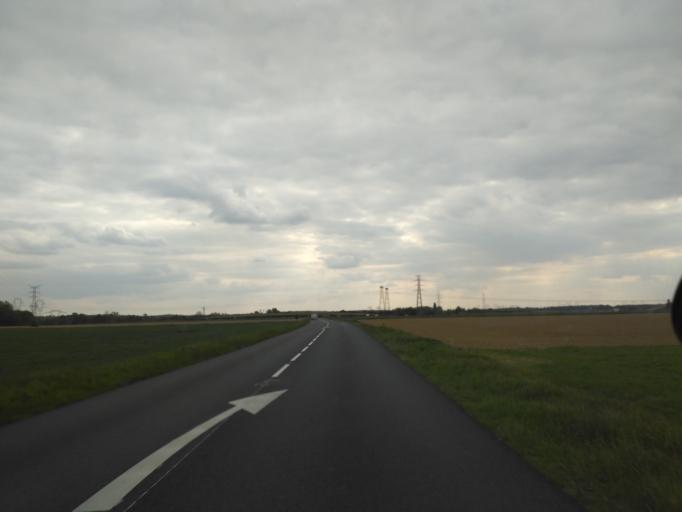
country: FR
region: Ile-de-France
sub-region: Departement de Seine-et-Marne
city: Moisenay
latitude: 48.5734
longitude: 2.7721
